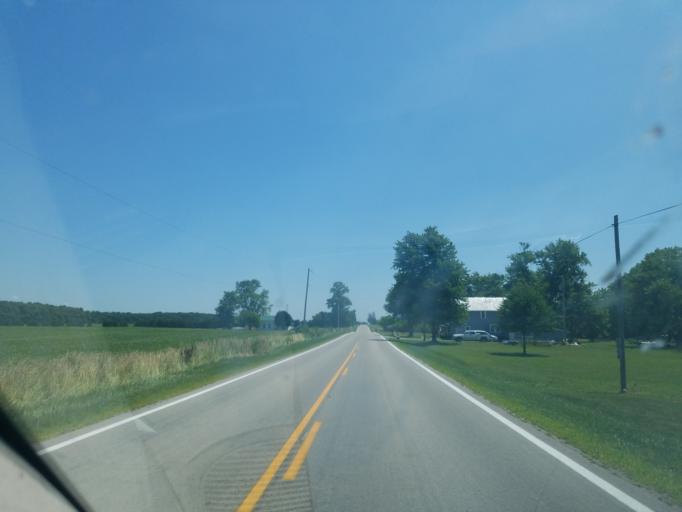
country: US
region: Ohio
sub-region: Mercer County
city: Rockford
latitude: 40.7424
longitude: -84.7270
